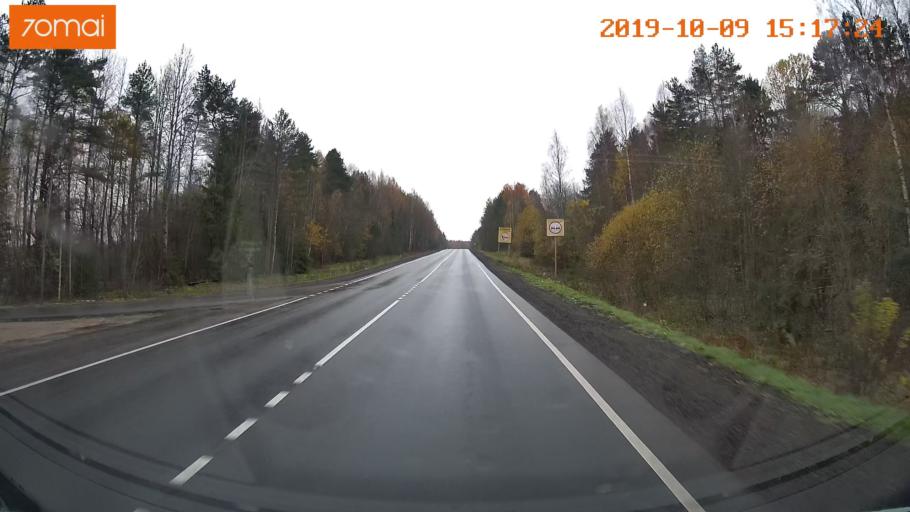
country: RU
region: Kostroma
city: Susanino
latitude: 58.0988
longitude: 41.5829
